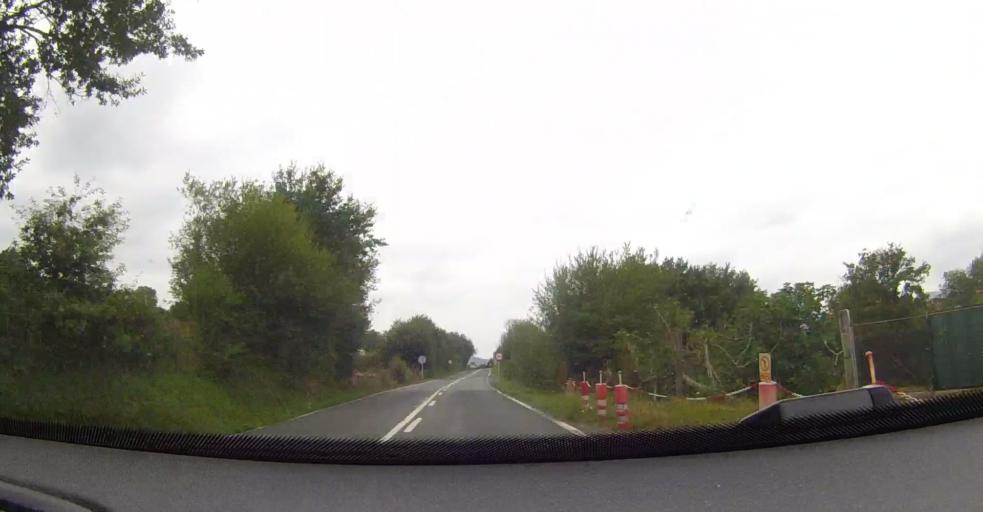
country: ES
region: Basque Country
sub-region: Bizkaia
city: Balmaseda
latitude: 43.2443
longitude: -3.2359
